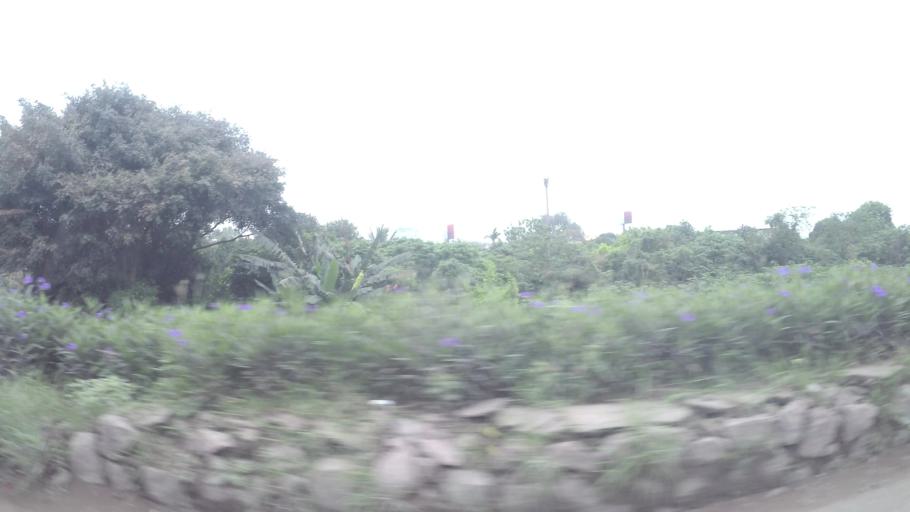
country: VN
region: Hung Yen
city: Van Giang
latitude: 20.9793
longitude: 105.8928
